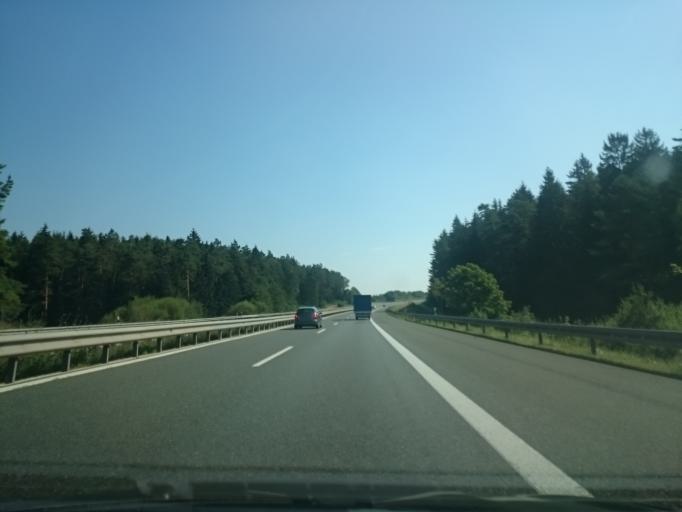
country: DE
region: Bavaria
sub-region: Upper Franconia
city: Stadelhofen
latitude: 49.9981
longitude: 11.1808
